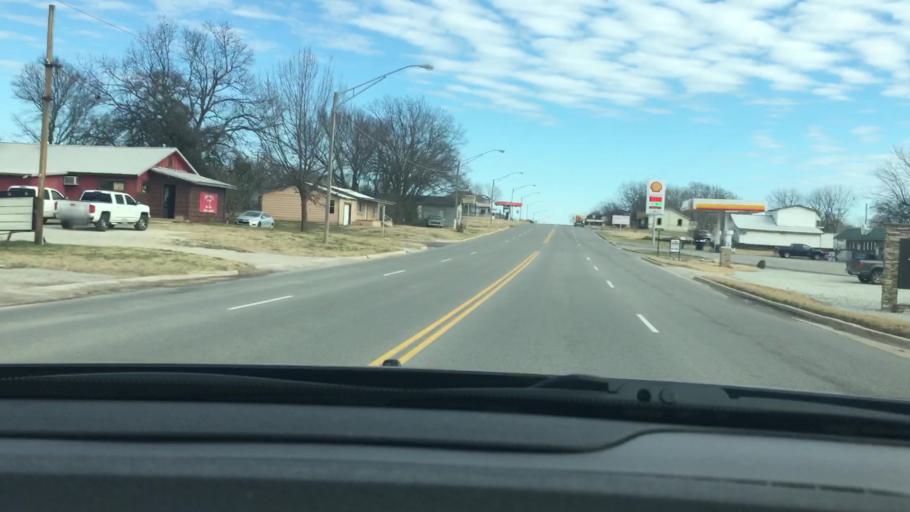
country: US
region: Oklahoma
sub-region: Garvin County
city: Stratford
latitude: 34.7966
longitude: -96.9563
